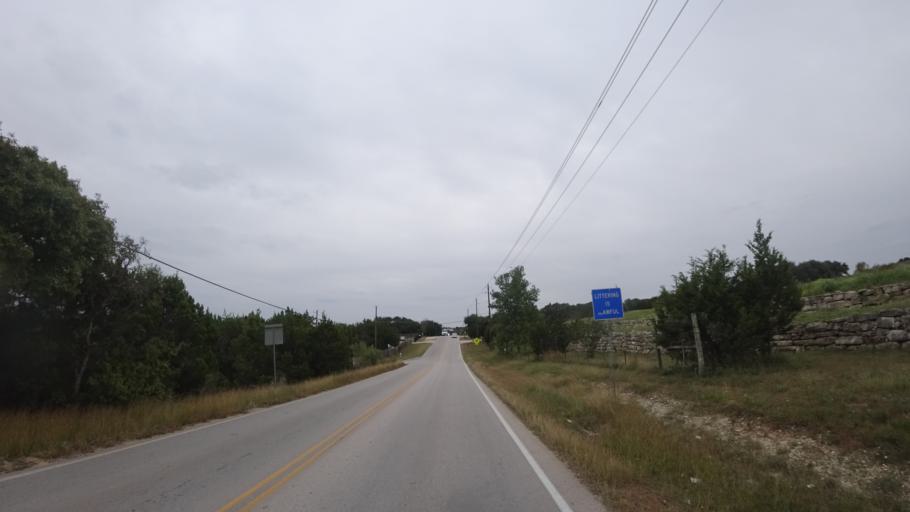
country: US
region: Texas
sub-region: Travis County
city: Lakeway
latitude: 30.3747
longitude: -97.9392
